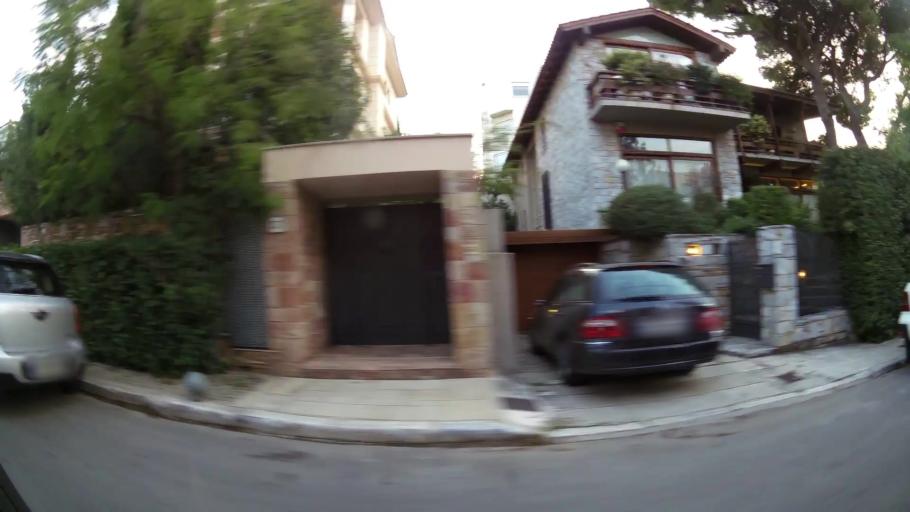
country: GR
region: Attica
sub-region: Nomarchia Athinas
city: Filothei
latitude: 38.0219
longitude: 23.7770
